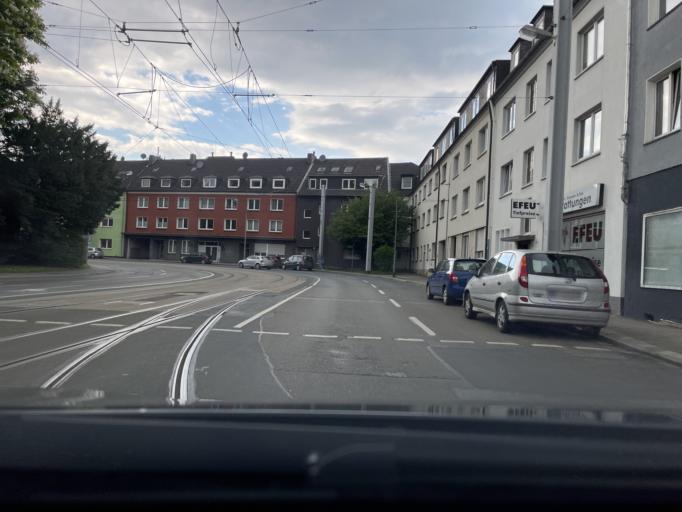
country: DE
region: North Rhine-Westphalia
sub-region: Regierungsbezirk Dusseldorf
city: Essen
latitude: 51.4792
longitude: 6.9765
